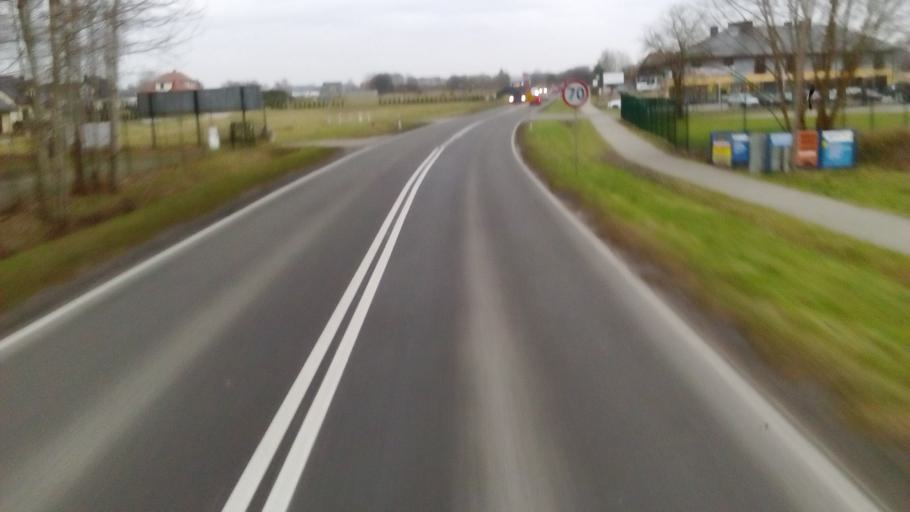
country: PL
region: West Pomeranian Voivodeship
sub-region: Powiat policki
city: Dobra
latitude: 53.4457
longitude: 14.4001
